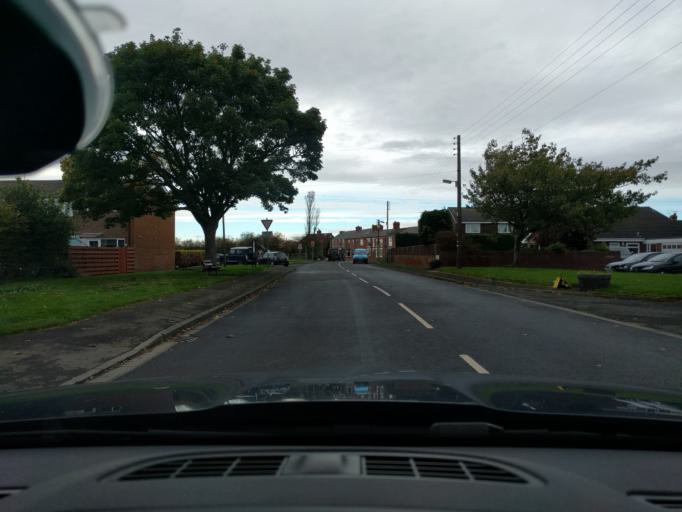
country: GB
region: England
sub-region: Northumberland
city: Ashington
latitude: 55.1446
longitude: -1.5484
